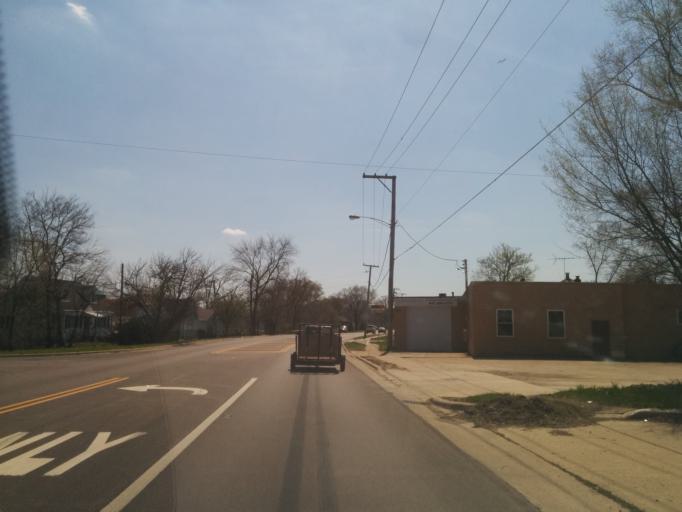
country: US
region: Illinois
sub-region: Kane County
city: South Elgin
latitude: 41.9994
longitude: -88.2974
